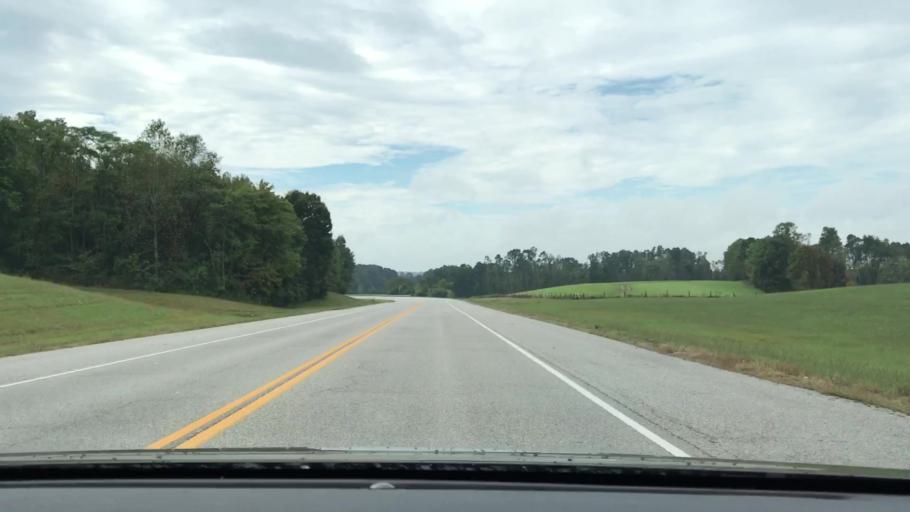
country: US
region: Tennessee
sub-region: Macon County
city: Red Boiling Springs
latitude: 36.5418
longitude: -85.8175
